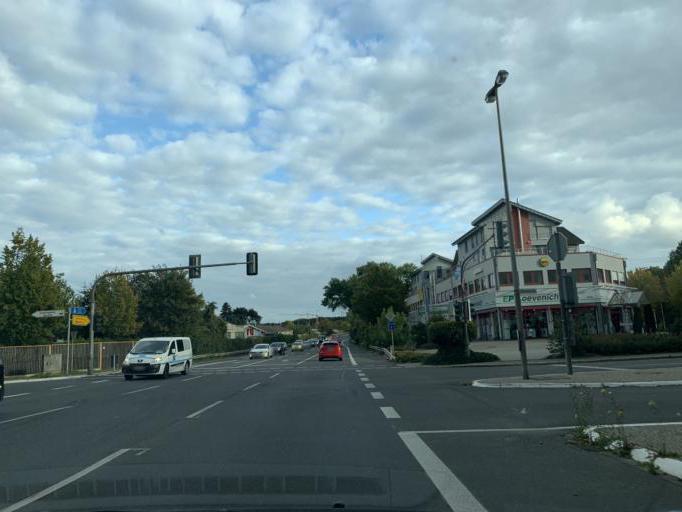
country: DE
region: North Rhine-Westphalia
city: Julich
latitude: 50.9095
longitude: 6.3568
